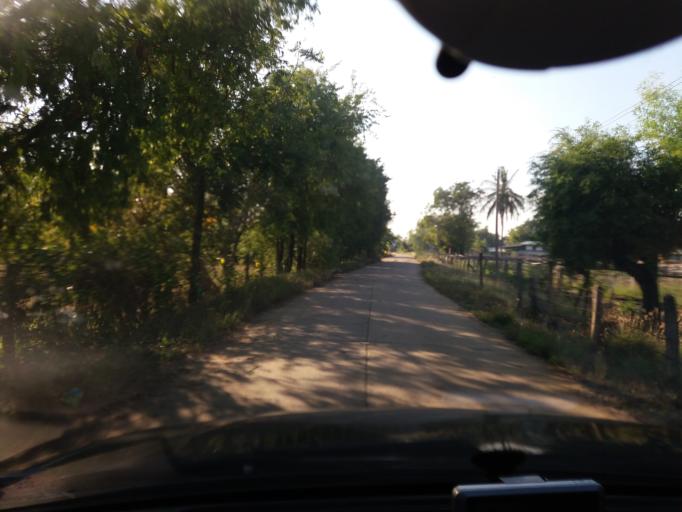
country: TH
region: Suphan Buri
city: Doem Bang Nang Buat
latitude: 14.9128
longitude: 100.1337
